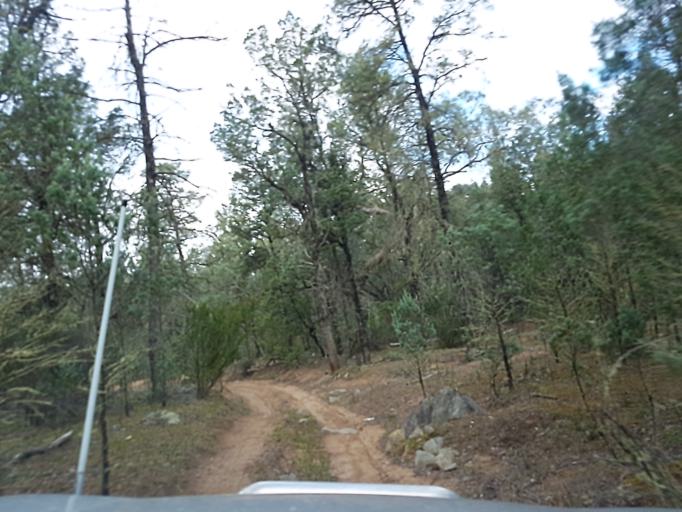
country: AU
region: New South Wales
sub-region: Snowy River
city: Jindabyne
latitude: -36.9444
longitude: 148.3873
